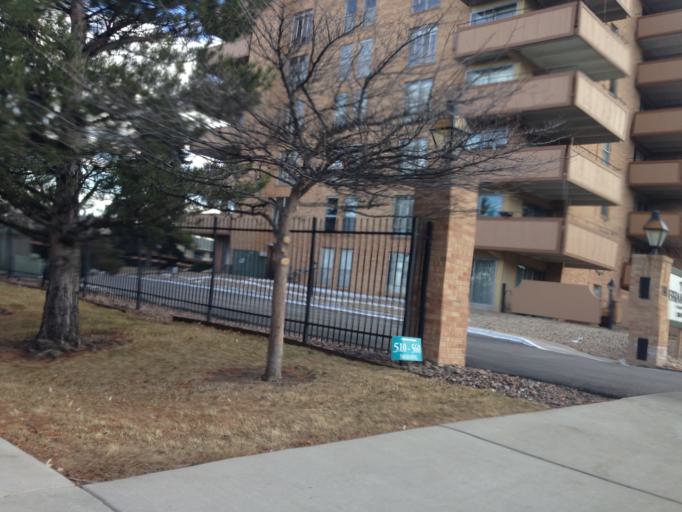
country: US
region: Colorado
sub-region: Boulder County
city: Boulder
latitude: 39.9973
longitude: -105.2363
